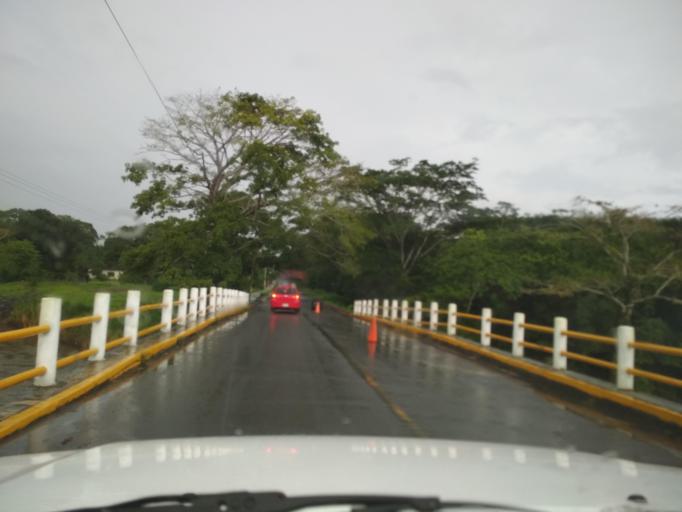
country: MX
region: Veracruz
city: Santiago Tuxtla
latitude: 18.4472
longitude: -95.3172
